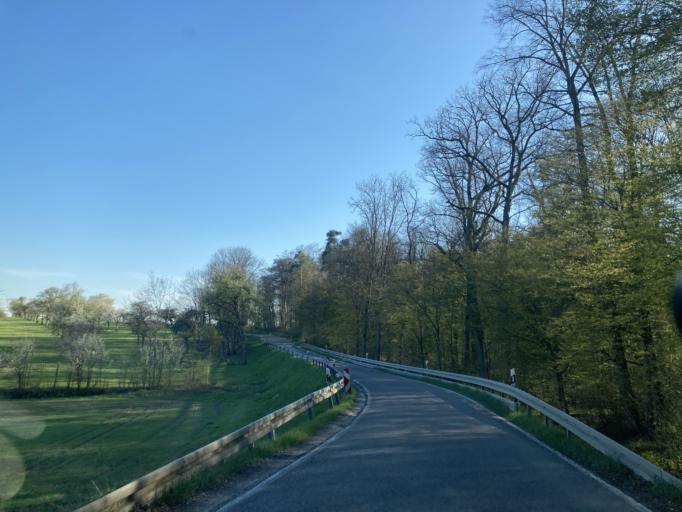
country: DE
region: Baden-Wuerttemberg
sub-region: Regierungsbezirk Stuttgart
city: Hildrizhausen
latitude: 48.5557
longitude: 8.9440
